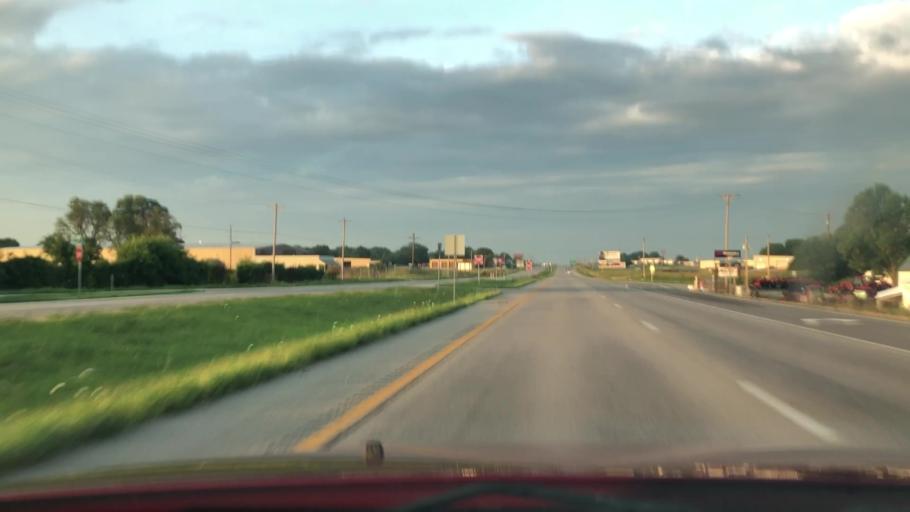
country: US
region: Missouri
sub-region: Greene County
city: Battlefield
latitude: 37.1537
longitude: -93.4137
